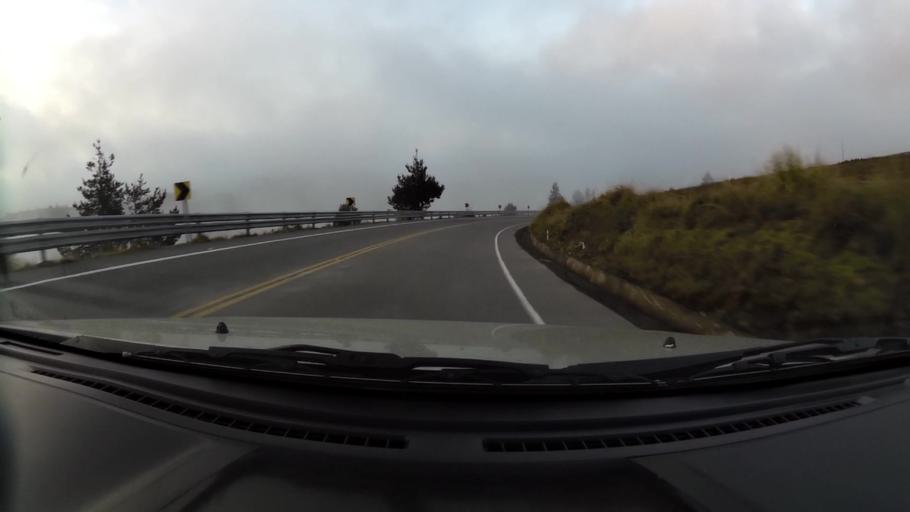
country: EC
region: Chimborazo
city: Alausi
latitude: -2.0956
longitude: -78.7488
